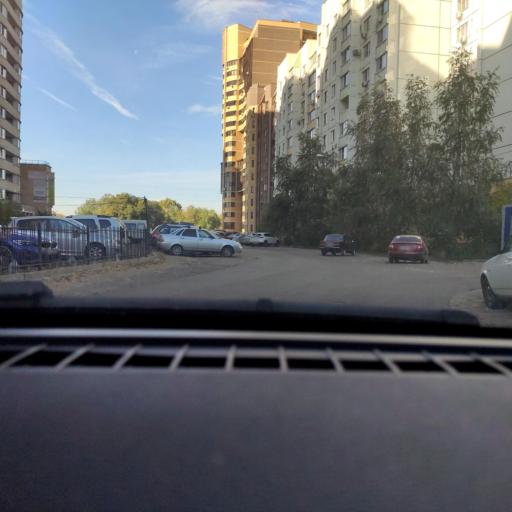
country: RU
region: Voronezj
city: Voronezh
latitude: 51.6474
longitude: 39.2356
